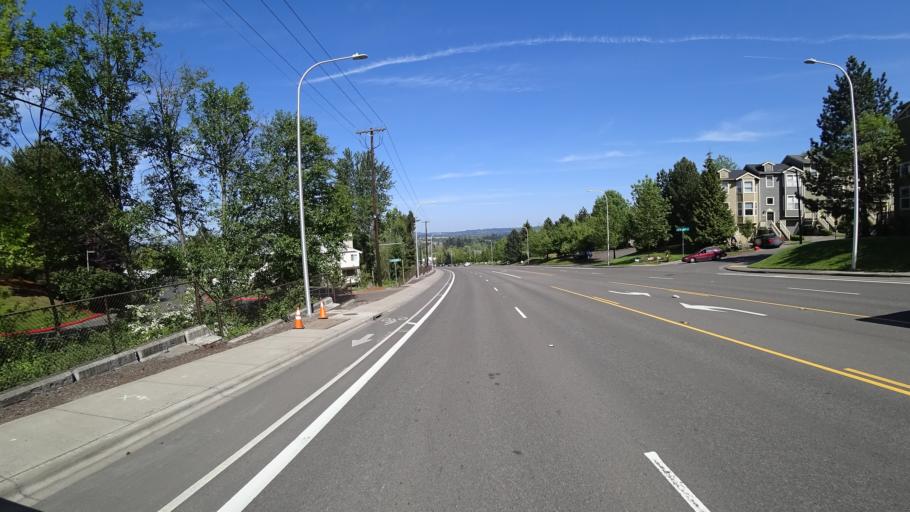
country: US
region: Oregon
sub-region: Washington County
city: King City
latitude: 45.4338
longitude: -122.8355
